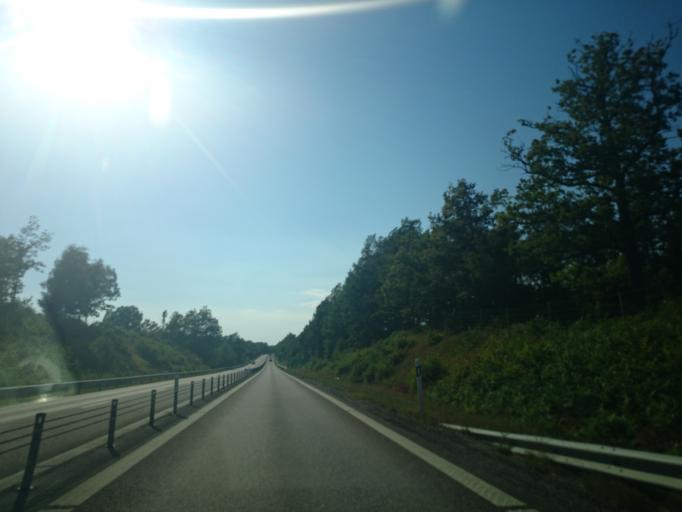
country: SE
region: Blekinge
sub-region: Ronneby Kommun
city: Kallinge
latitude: 56.2043
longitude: 15.3457
